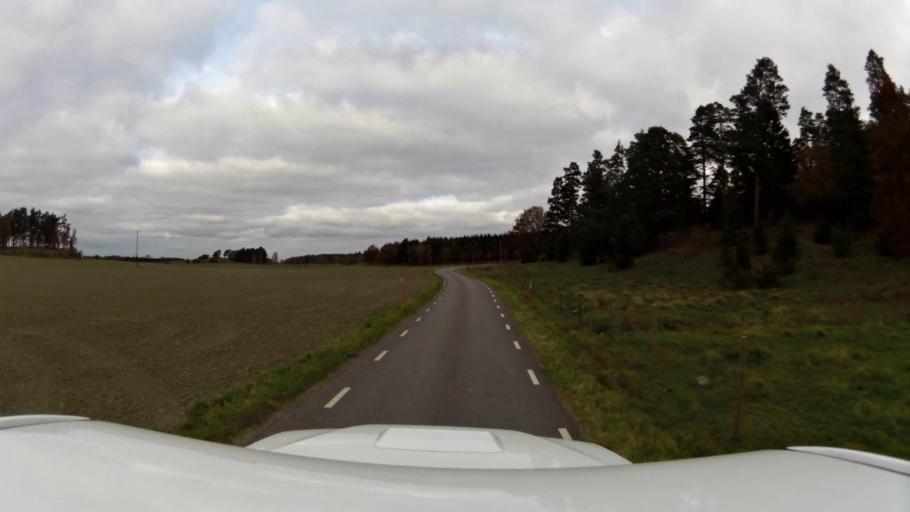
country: SE
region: OEstergoetland
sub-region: Linkopings Kommun
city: Linghem
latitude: 58.3791
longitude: 15.8208
